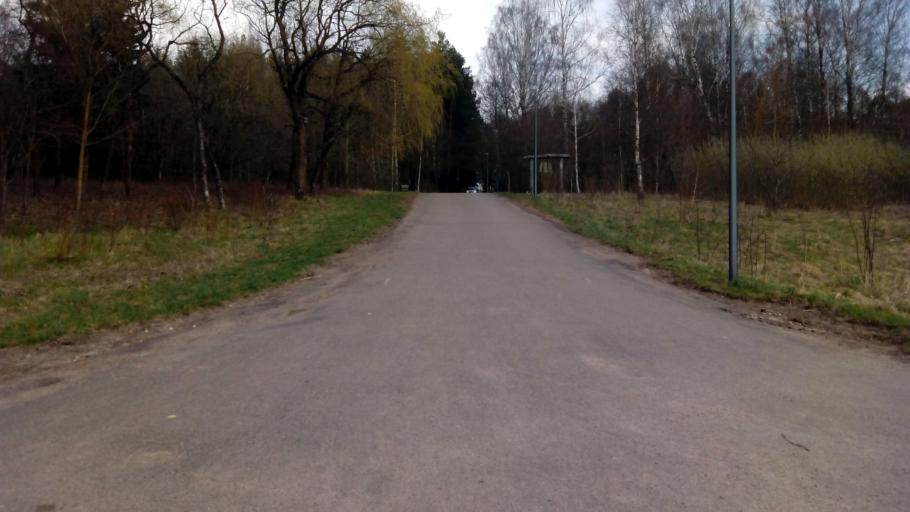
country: LT
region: Siauliu apskritis
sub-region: Siauliai
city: Siauliai
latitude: 55.9322
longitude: 23.3372
